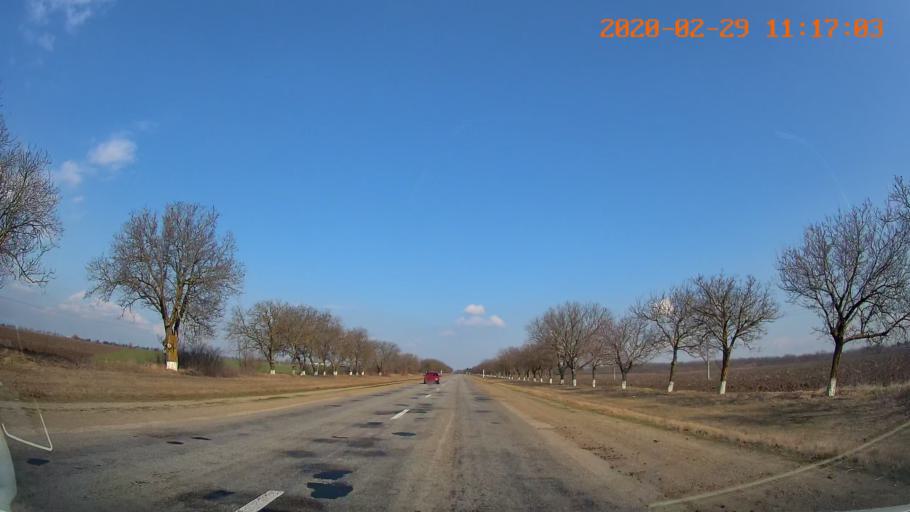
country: MD
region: Telenesti
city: Dubasari
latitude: 47.3169
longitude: 29.1695
